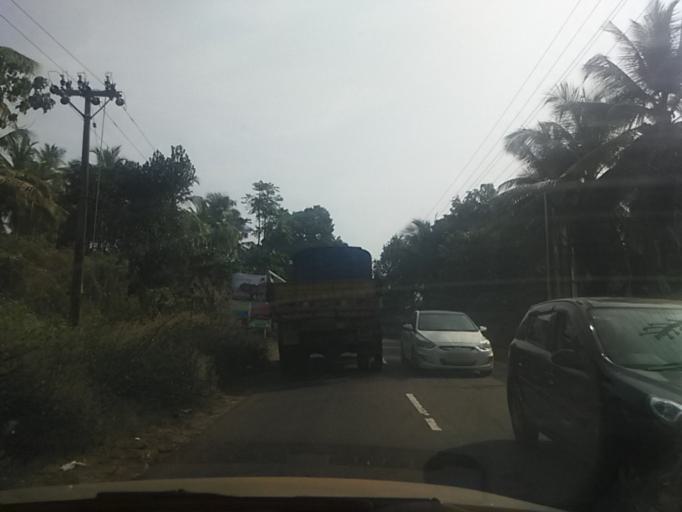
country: IN
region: Kerala
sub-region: Kozhikode
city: Kunnamangalam
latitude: 11.3121
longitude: 75.9184
